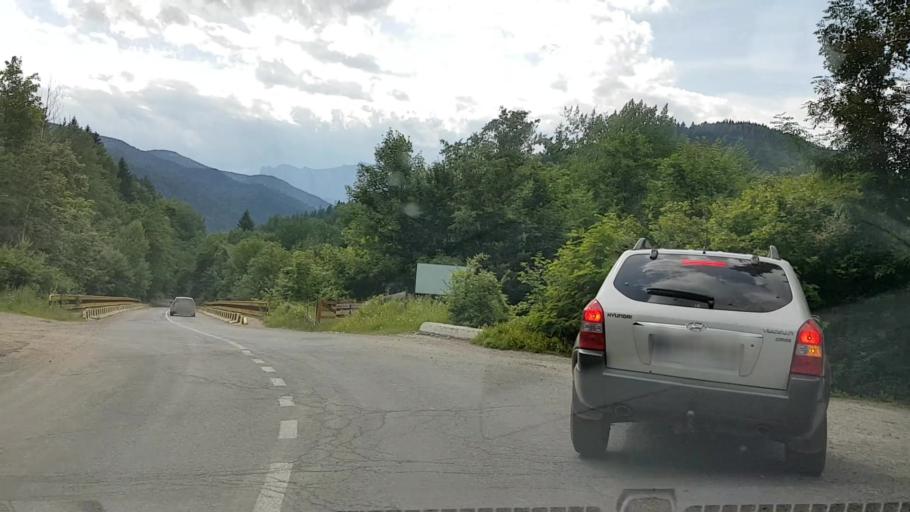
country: RO
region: Neamt
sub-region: Comuna Bicaz
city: Dodeni
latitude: 46.9383
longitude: 26.1121
